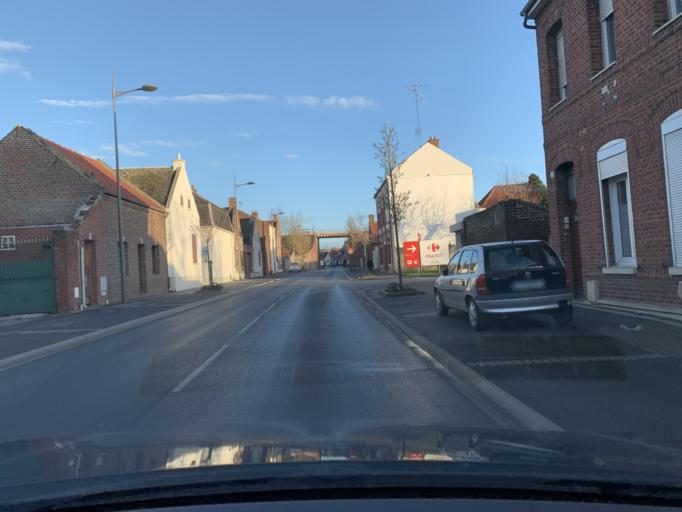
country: FR
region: Nord-Pas-de-Calais
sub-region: Departement du Nord
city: Cambrai
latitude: 50.1642
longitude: 3.2509
